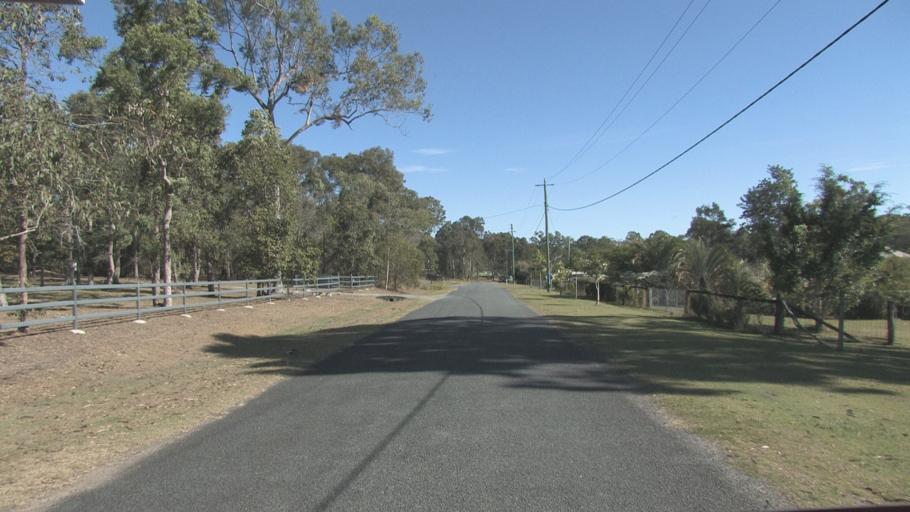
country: AU
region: Queensland
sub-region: Ipswich
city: Springfield Lakes
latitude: -27.7122
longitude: 152.9560
